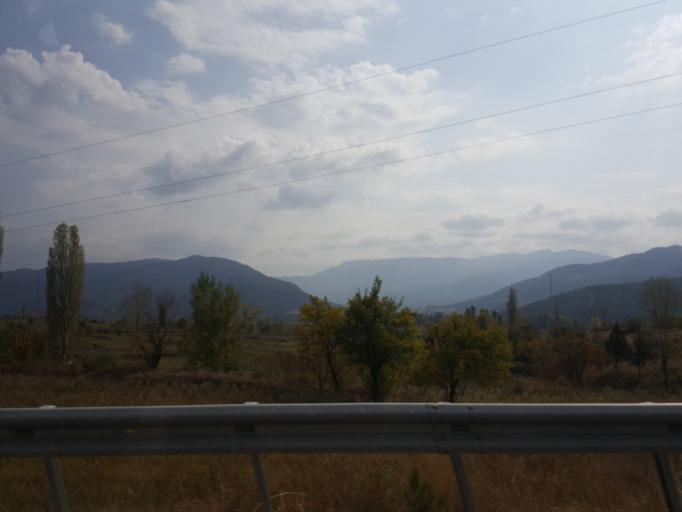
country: TR
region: Corum
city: Hacihamza
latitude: 41.1141
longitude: 34.3987
